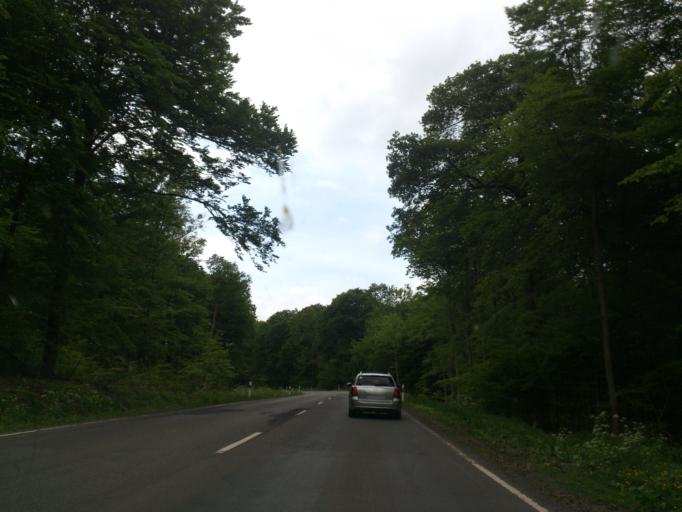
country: DE
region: Hesse
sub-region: Regierungsbezirk Kassel
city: Calden
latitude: 51.3498
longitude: 9.4119
